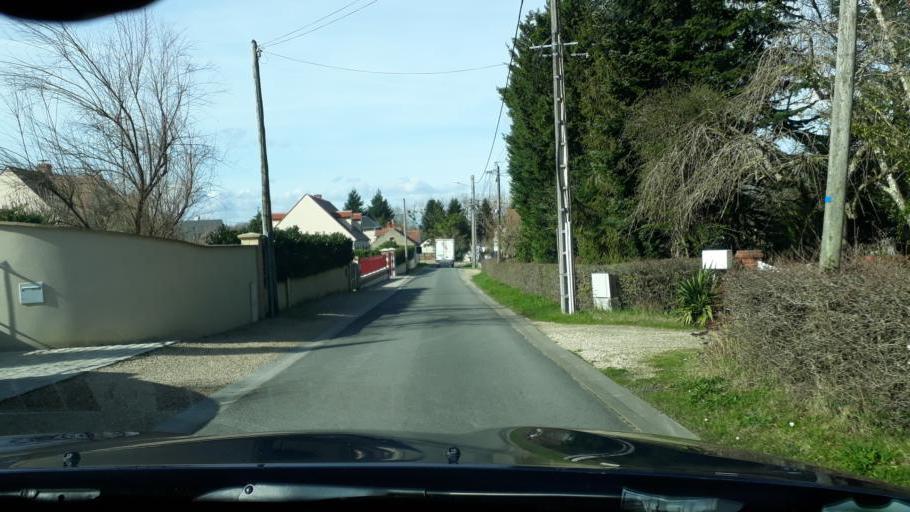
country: FR
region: Centre
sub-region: Departement du Loiret
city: Donnery
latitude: 47.9127
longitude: 2.1090
